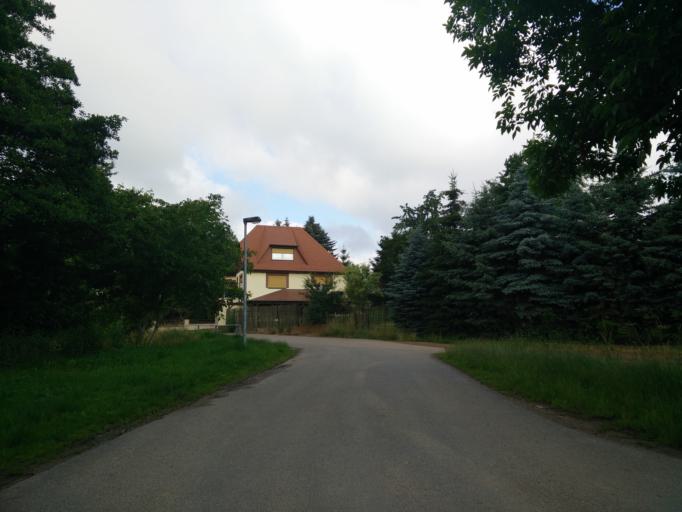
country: DE
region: Saxony
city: Geithain
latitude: 51.0507
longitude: 12.6987
